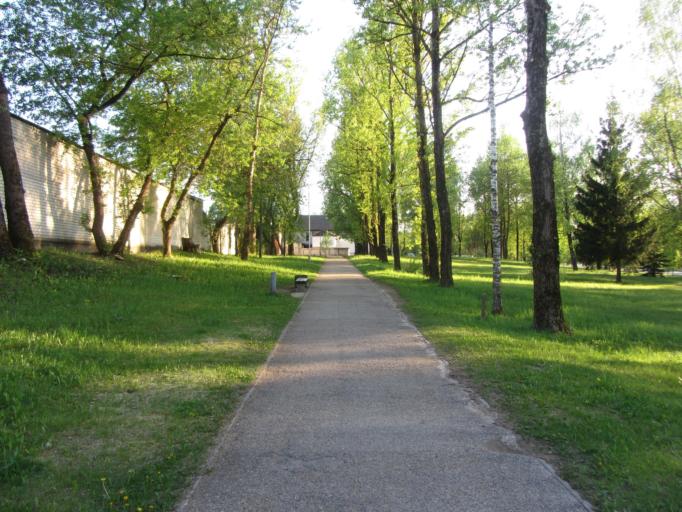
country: LT
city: Moletai
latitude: 55.2231
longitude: 25.4071
